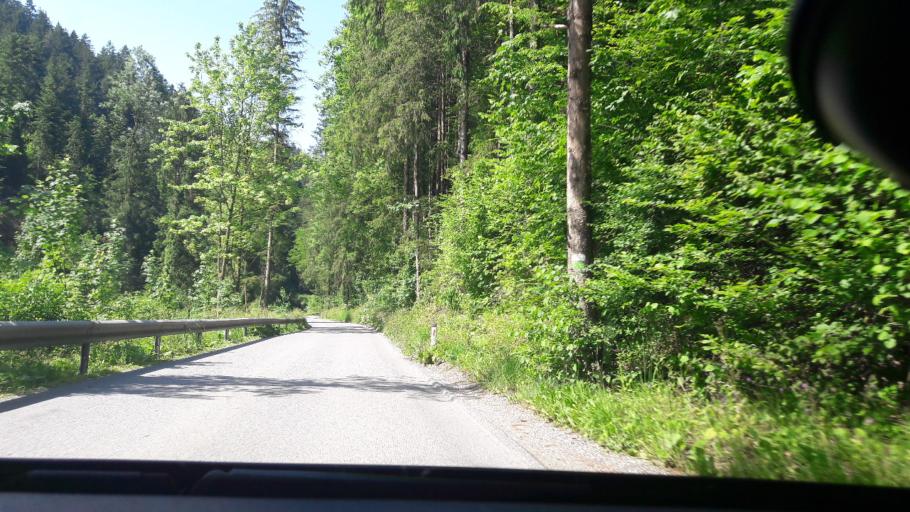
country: AT
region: Styria
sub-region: Politischer Bezirk Voitsberg
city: Kohlschwarz
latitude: 47.1134
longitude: 15.1298
